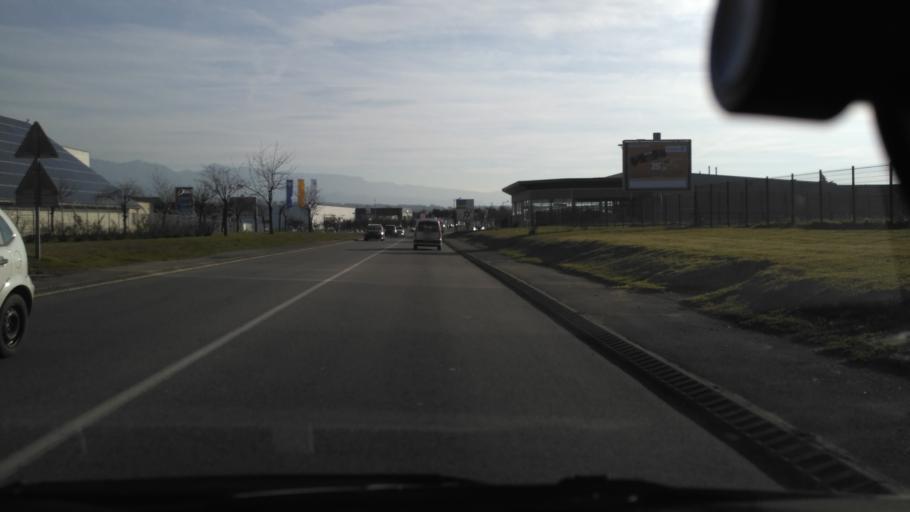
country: FR
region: Rhone-Alpes
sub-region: Departement de la Drome
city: Bourg-de-Peage
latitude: 45.0466
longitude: 5.0840
